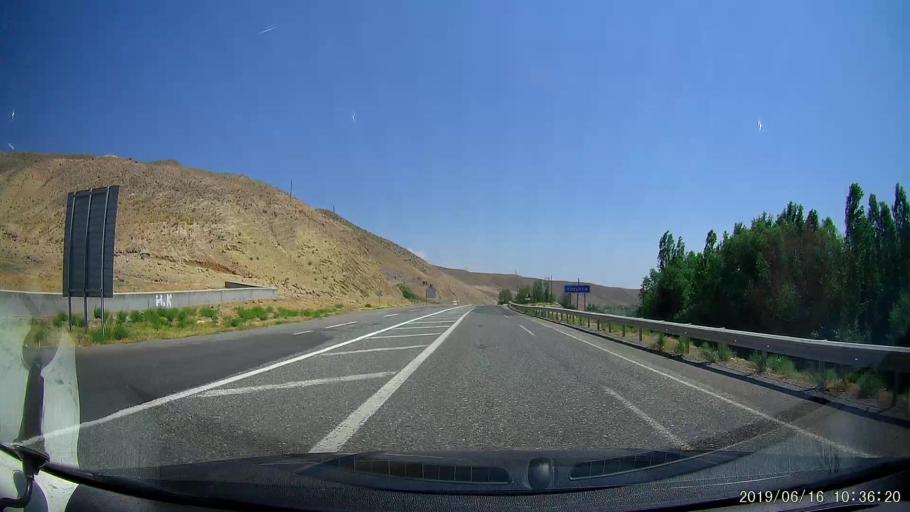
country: TR
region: Igdir
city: Tuzluca
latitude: 40.0369
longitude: 43.6792
